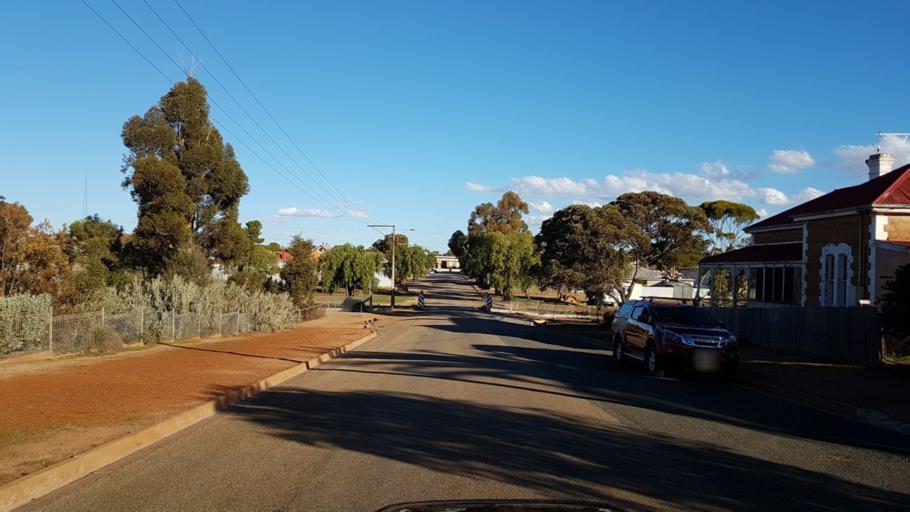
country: AU
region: South Australia
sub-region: Peterborough
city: Peterborough
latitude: -32.9706
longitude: 138.8361
